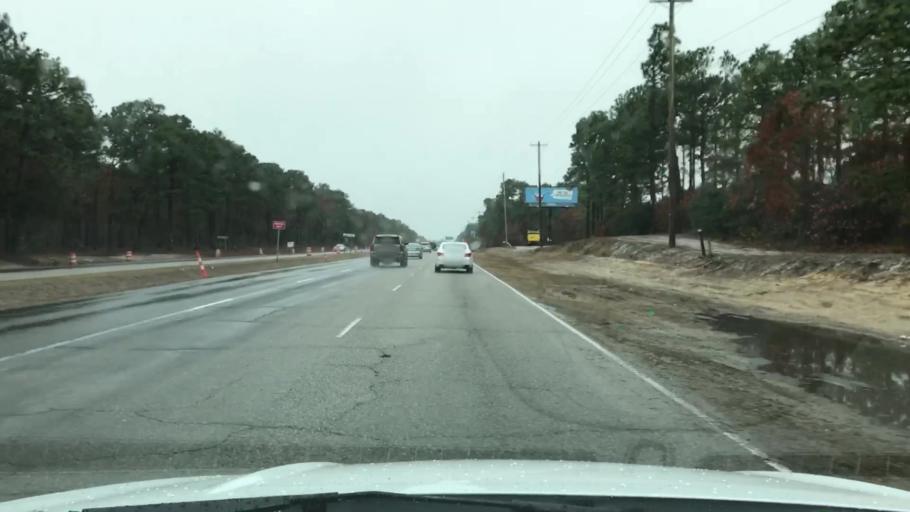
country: US
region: South Carolina
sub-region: Horry County
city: Myrtle Beach
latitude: 33.7538
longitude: -78.8283
